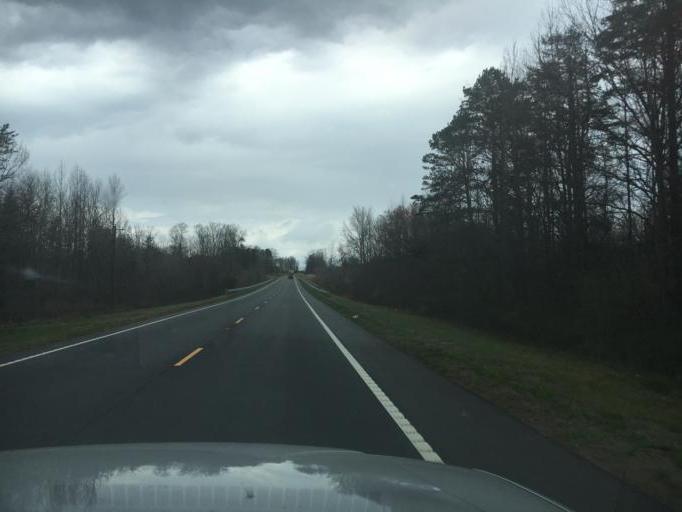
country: US
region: South Carolina
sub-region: Oconee County
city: Walhalla
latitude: 34.7941
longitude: -83.0255
